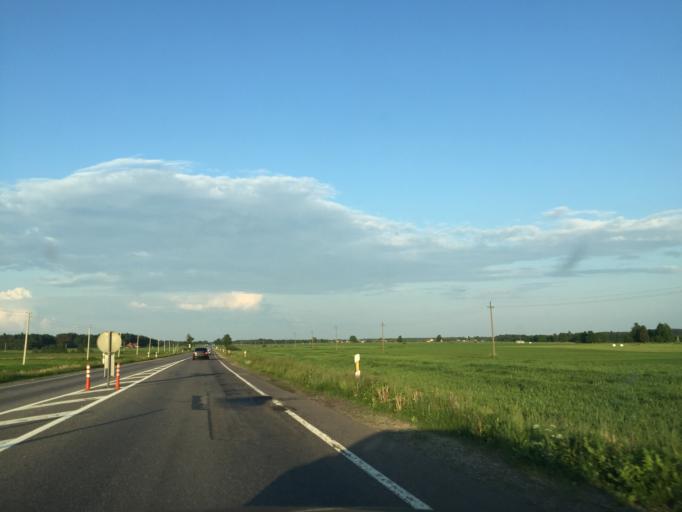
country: LT
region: Telsiu apskritis
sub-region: Telsiai
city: Telsiai
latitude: 56.0005
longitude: 22.4619
